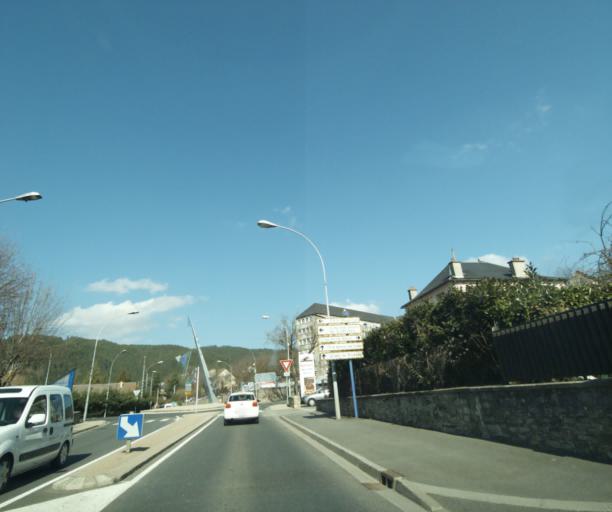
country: FR
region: Languedoc-Roussillon
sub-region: Departement de la Lozere
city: Mende
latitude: 44.5204
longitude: 3.5105
